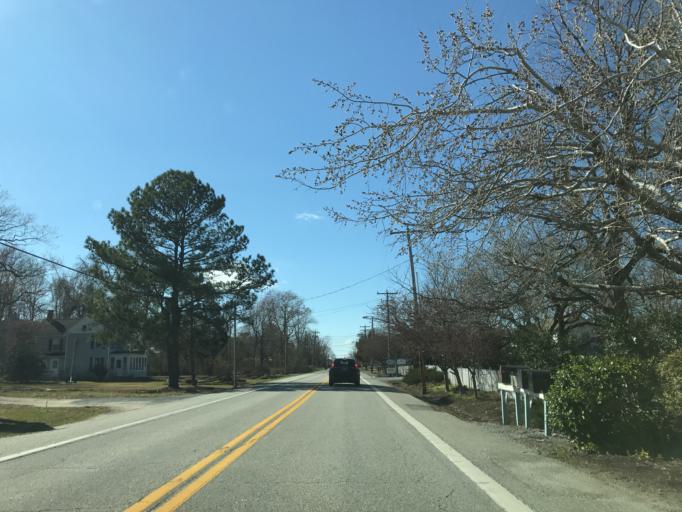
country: US
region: Maryland
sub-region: Kent County
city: Rock Hall
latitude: 39.1399
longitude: -76.2498
